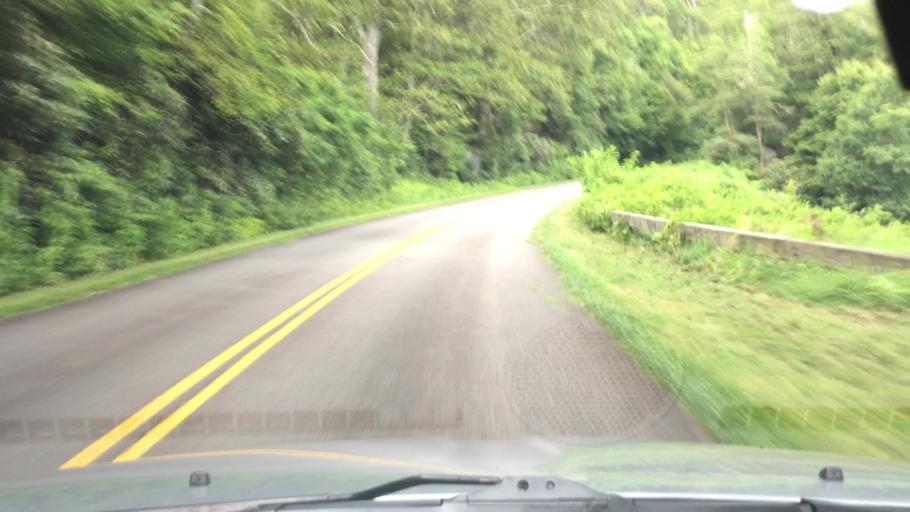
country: US
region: North Carolina
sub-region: Buncombe County
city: Black Mountain
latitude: 35.7182
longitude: -82.2275
